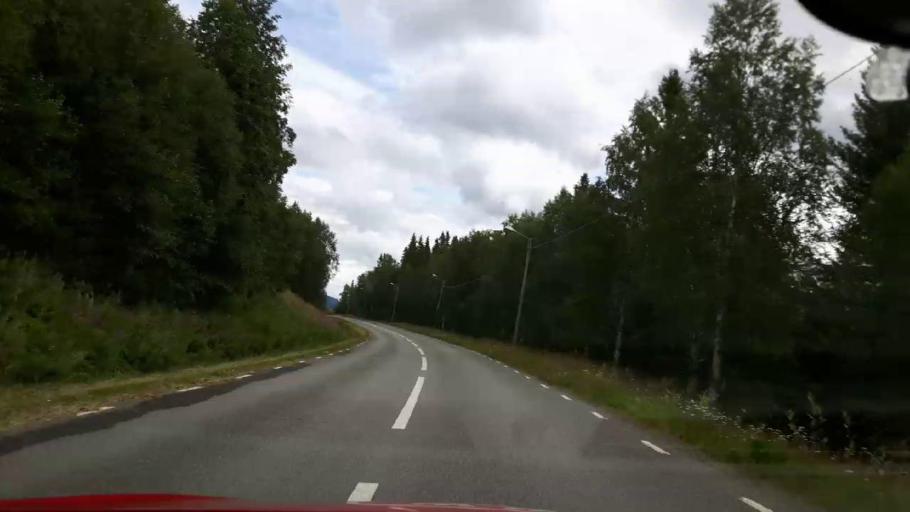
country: NO
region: Nord-Trondelag
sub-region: Lierne
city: Sandvika
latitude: 64.3903
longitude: 14.3793
